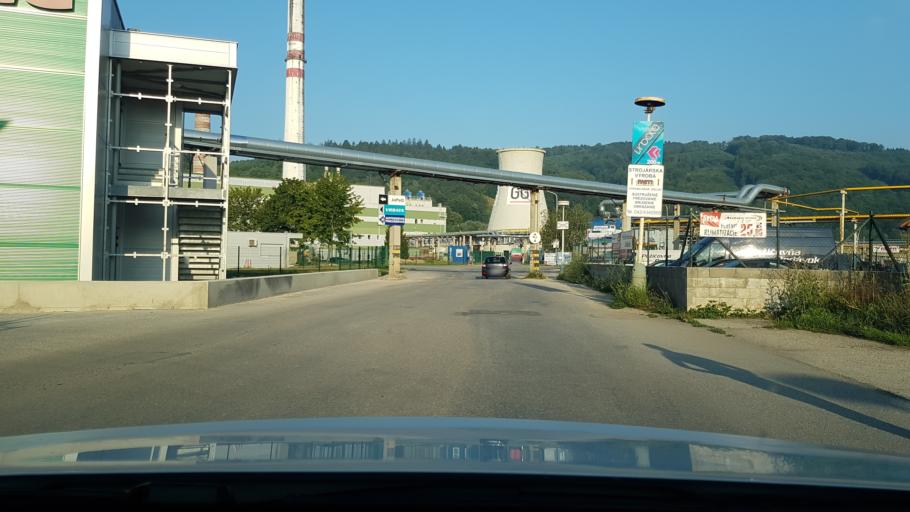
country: SK
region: Trenciansky
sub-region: Okres Povazska Bystrica
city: Povazska Bystrica
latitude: 49.1187
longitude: 18.4226
